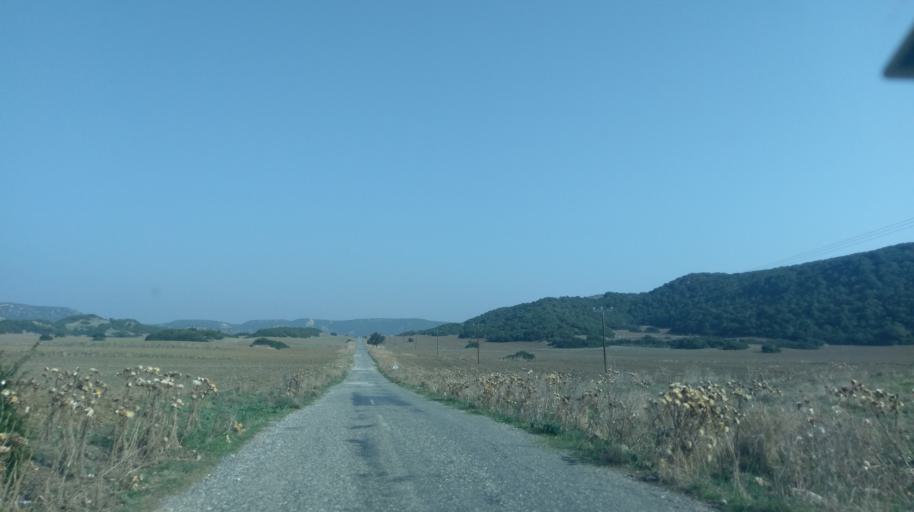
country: CY
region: Ammochostos
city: Rizokarpaso
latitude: 35.6392
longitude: 34.5172
